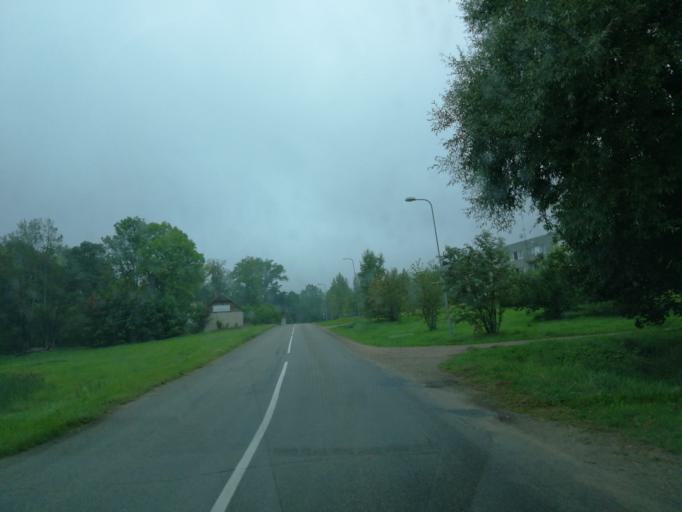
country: LV
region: Preilu Rajons
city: Jaunaglona
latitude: 56.2740
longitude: 27.0449
